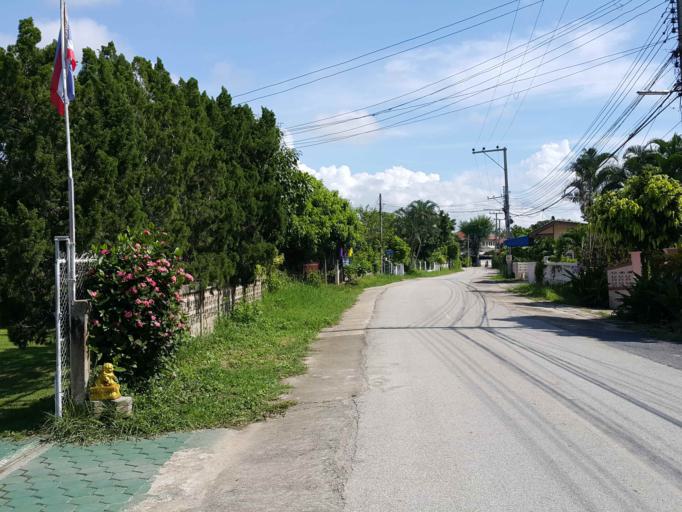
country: TH
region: Chiang Mai
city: San Kamphaeng
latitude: 18.8083
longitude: 99.1039
